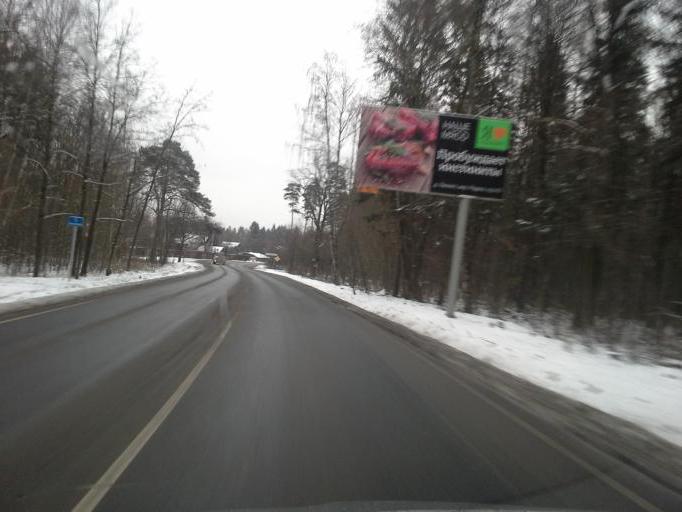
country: RU
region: Moskovskaya
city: Gorki Vtoryye
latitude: 55.6887
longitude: 37.1355
